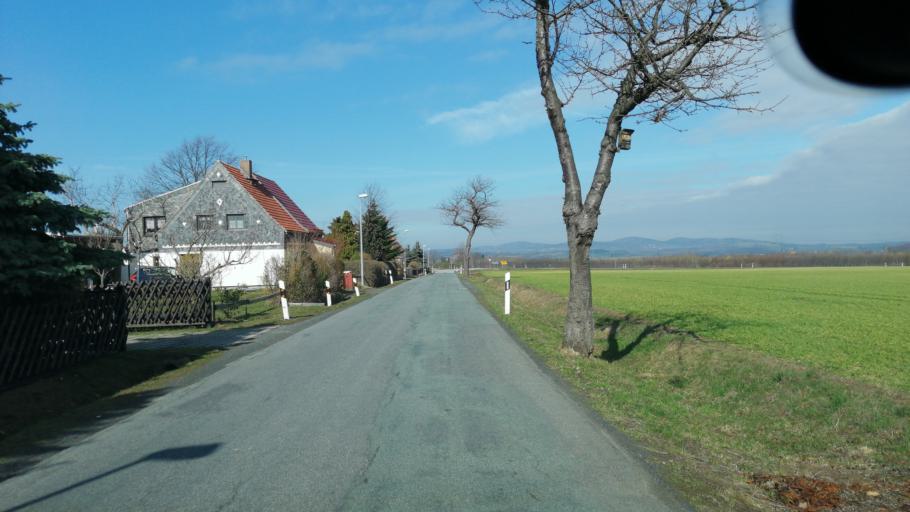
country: DE
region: Saxony
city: Niedercunnersdorf
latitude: 51.0302
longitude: 14.6838
